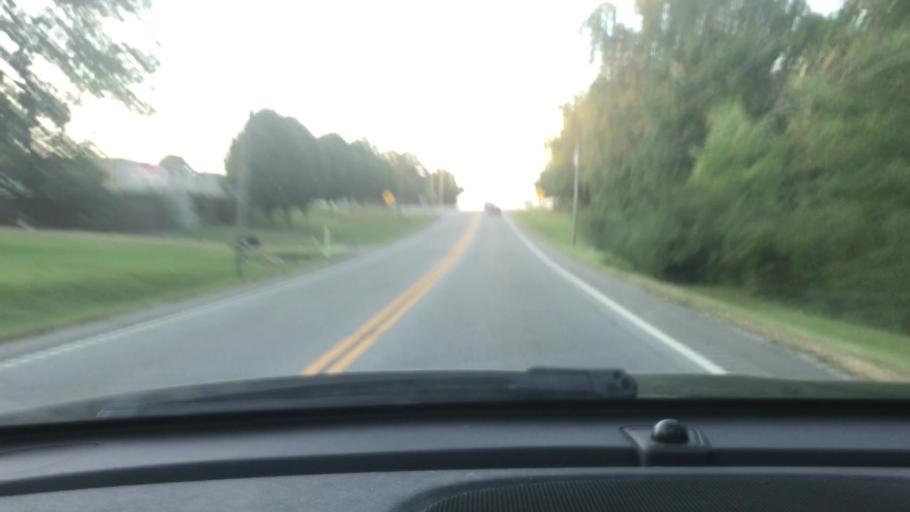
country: US
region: Tennessee
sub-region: Dickson County
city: Dickson
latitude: 36.1059
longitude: -87.3731
